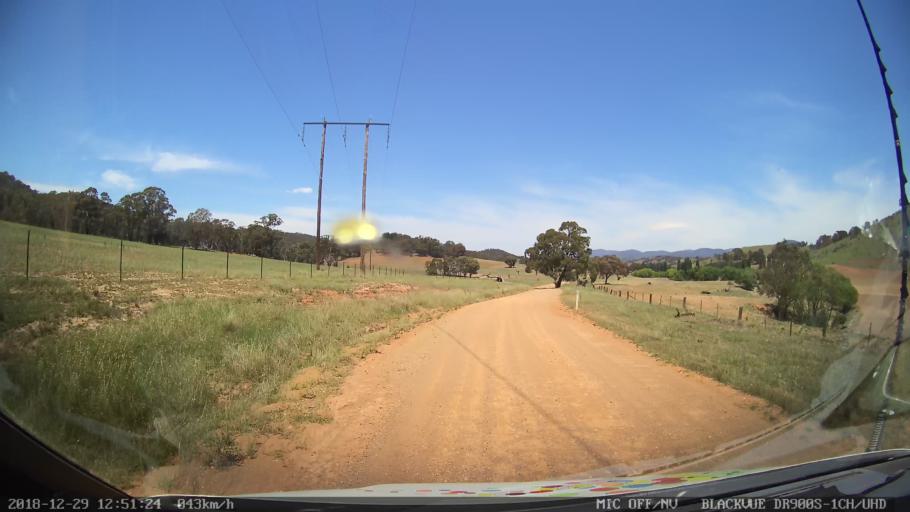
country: AU
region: Australian Capital Territory
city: Macarthur
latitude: -35.6747
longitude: 149.1989
